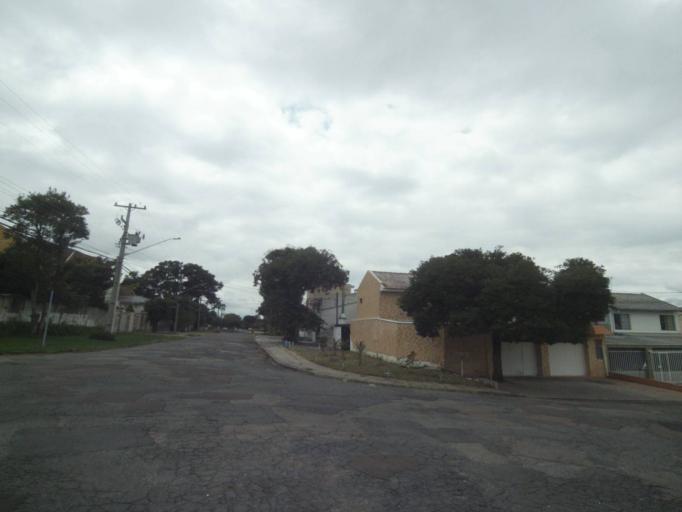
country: BR
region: Parana
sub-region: Pinhais
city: Pinhais
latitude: -25.4562
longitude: -49.2148
